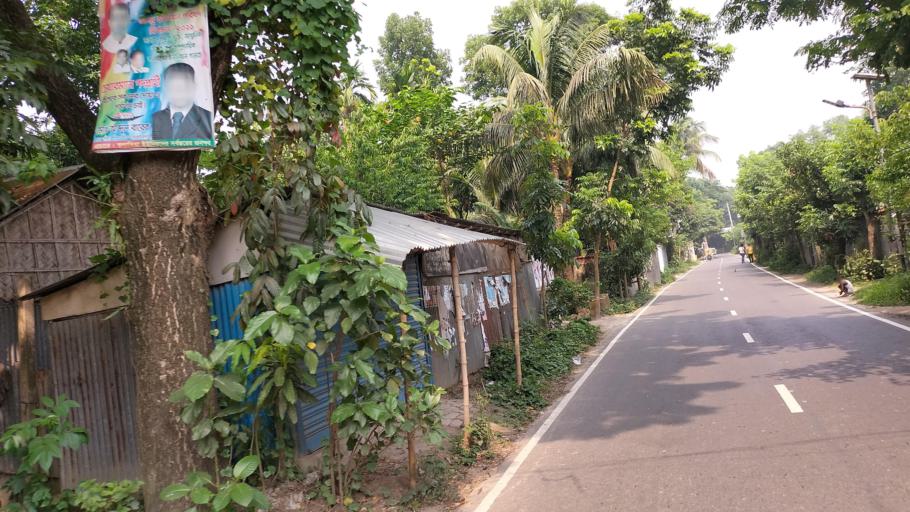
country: BD
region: Dhaka
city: Azimpur
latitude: 23.6964
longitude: 90.2968
